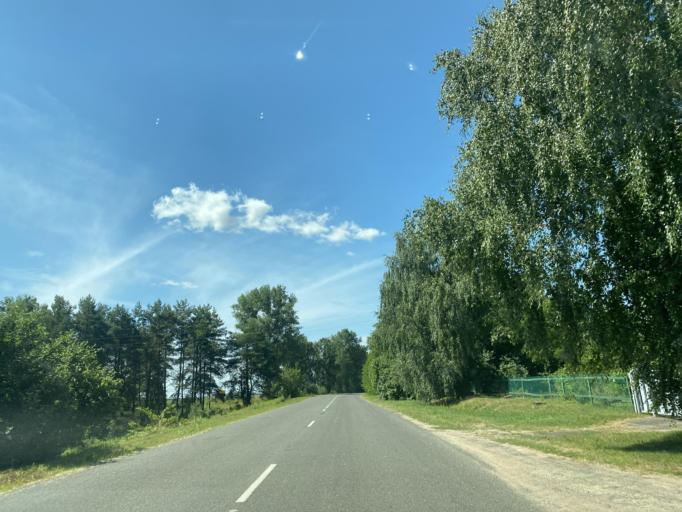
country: BY
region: Brest
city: Ivanava
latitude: 52.1810
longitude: 25.6031
